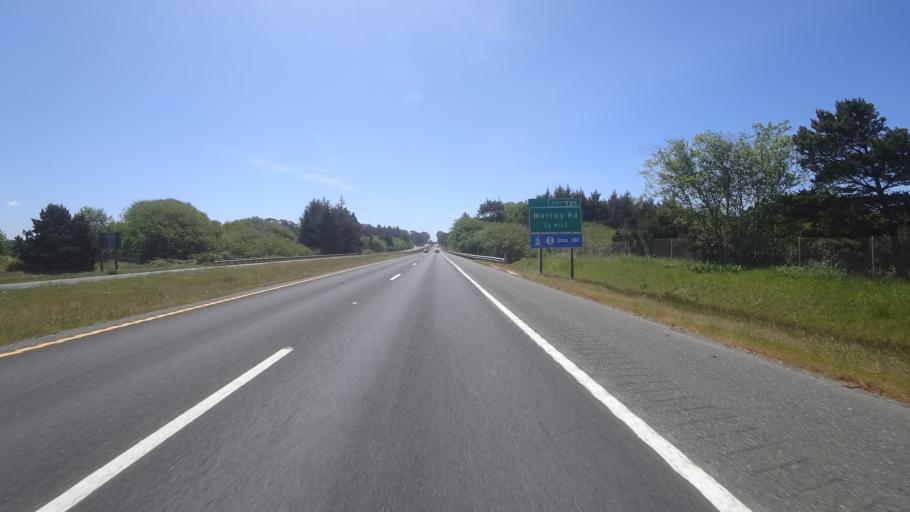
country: US
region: California
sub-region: Humboldt County
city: McKinleyville
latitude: 40.9636
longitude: -124.1162
